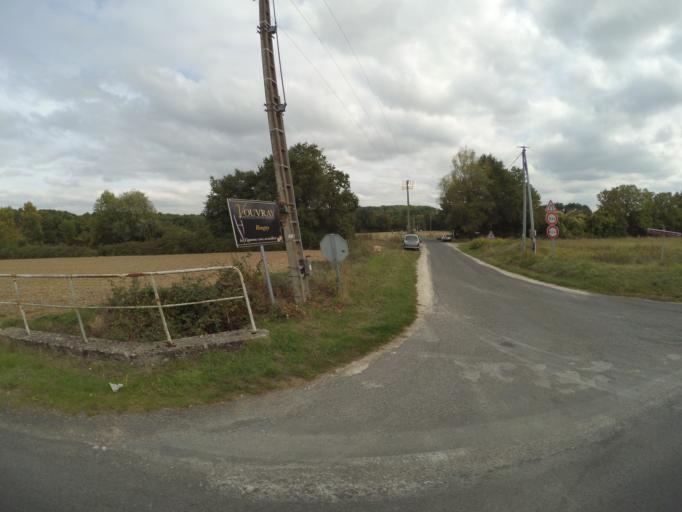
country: FR
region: Centre
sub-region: Departement d'Indre-et-Loire
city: Reugny
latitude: 47.4618
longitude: 0.8789
